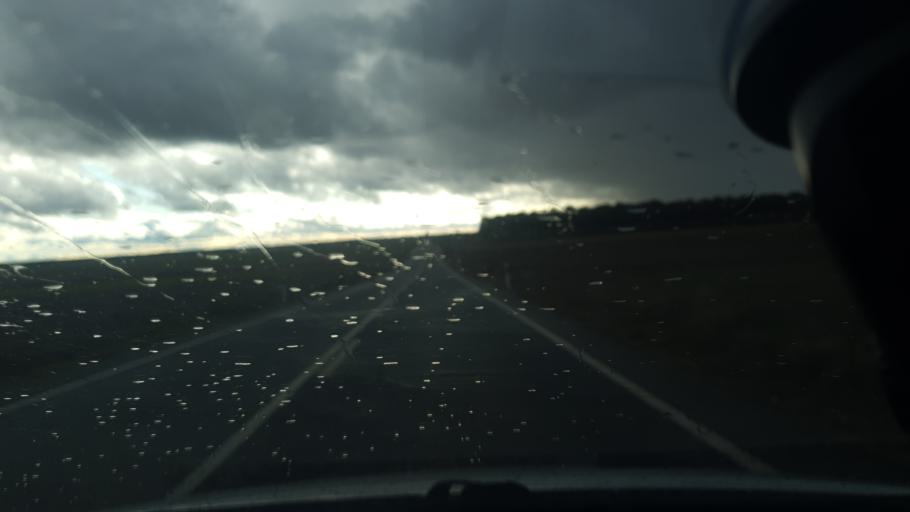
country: ES
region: Castille and Leon
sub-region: Provincia de Segovia
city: Chane
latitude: 41.3134
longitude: -4.3922
